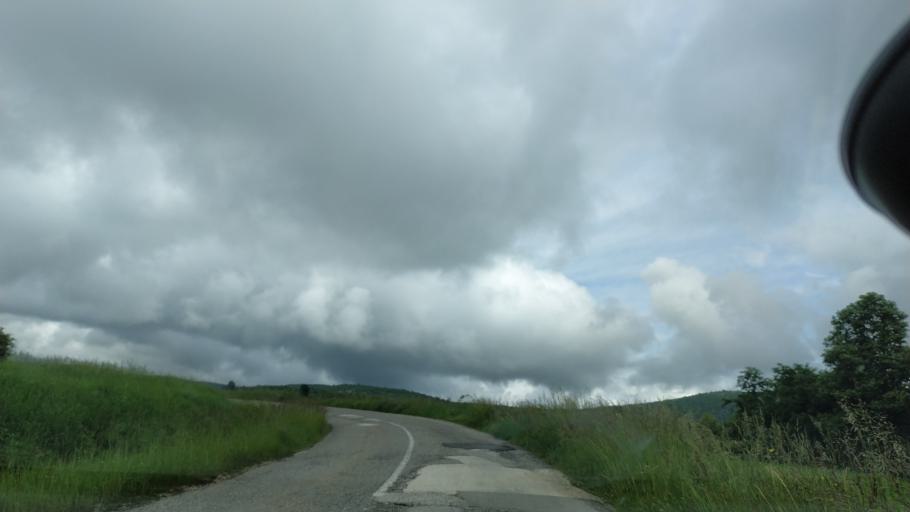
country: RS
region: Central Serbia
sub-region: Zajecarski Okrug
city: Soko Banja
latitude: 43.6981
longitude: 21.9391
